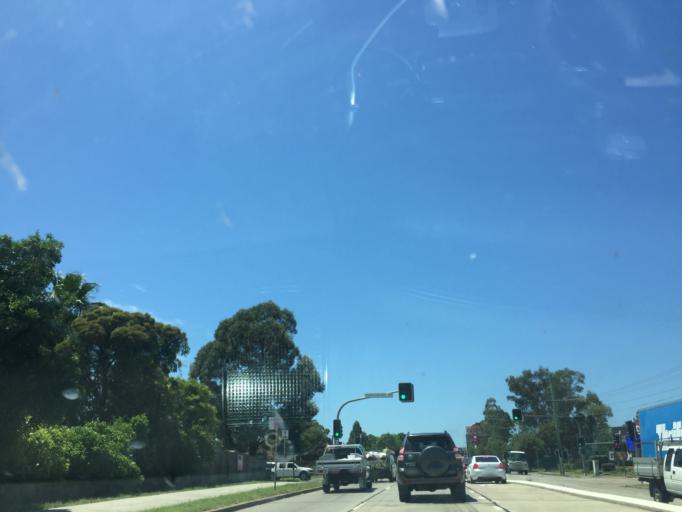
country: AU
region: New South Wales
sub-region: Blacktown
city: Glendenning
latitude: -33.7352
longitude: 150.8513
